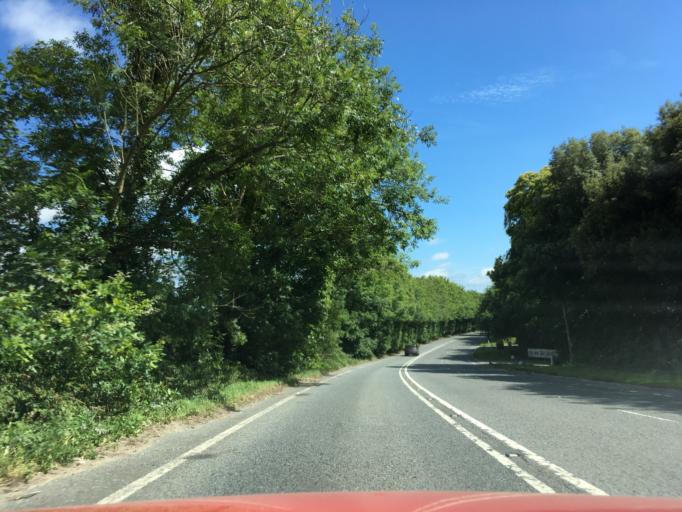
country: GB
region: England
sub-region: Dorset
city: Dorchester
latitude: 50.7649
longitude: -2.5301
